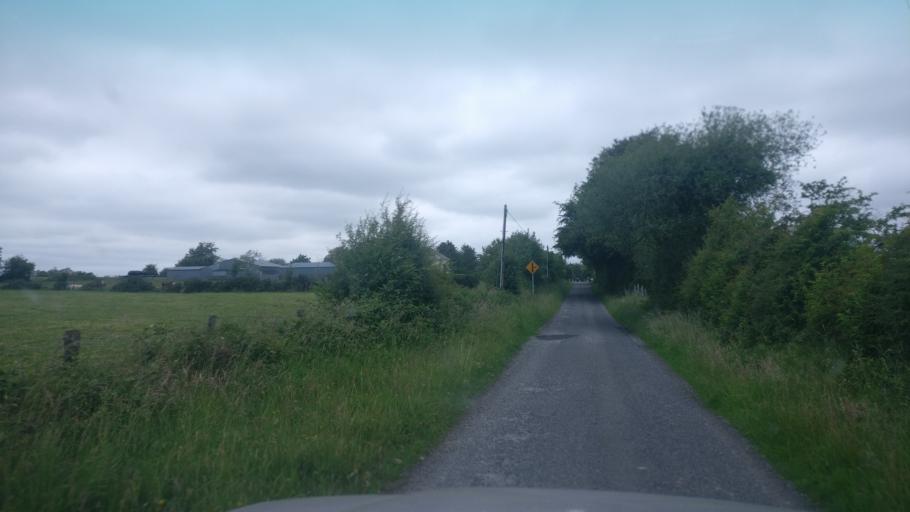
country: IE
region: Connaught
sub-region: County Galway
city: Ballinasloe
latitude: 53.3038
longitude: -8.3614
